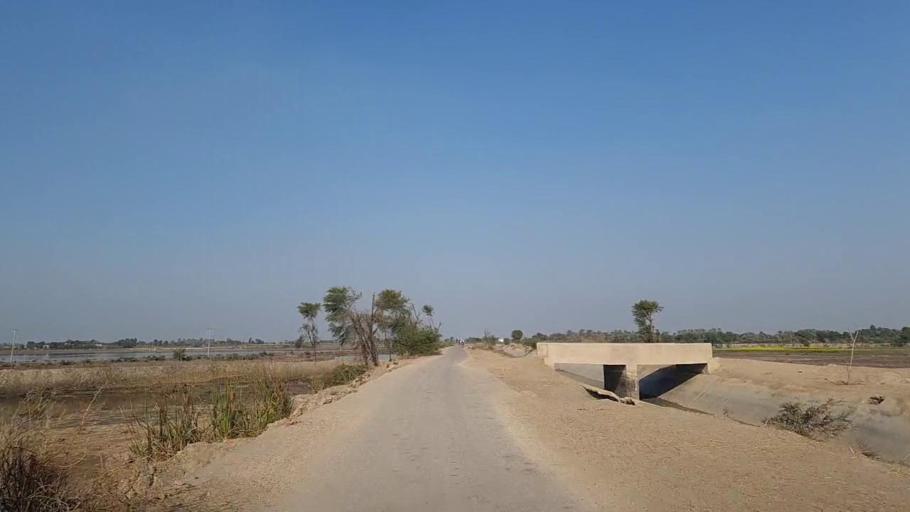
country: PK
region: Sindh
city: Daur
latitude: 26.4289
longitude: 68.2649
